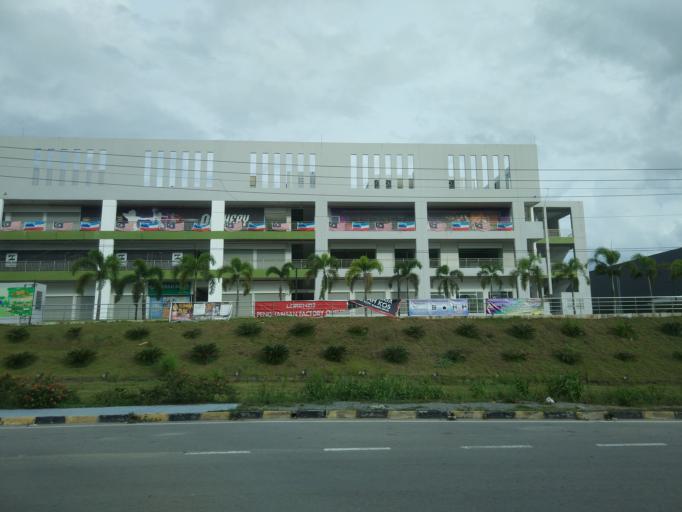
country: MY
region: Sabah
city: Kota Kinabalu
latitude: 6.0621
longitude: 116.1796
